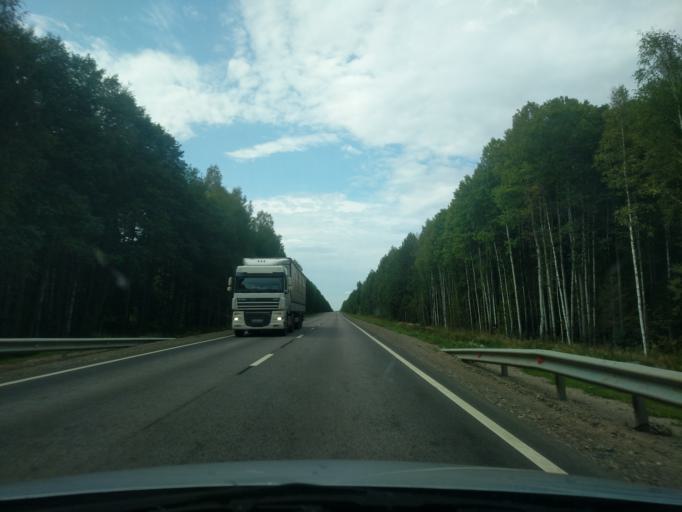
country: RU
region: Kostroma
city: Kadyy
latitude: 57.7956
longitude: 42.9331
